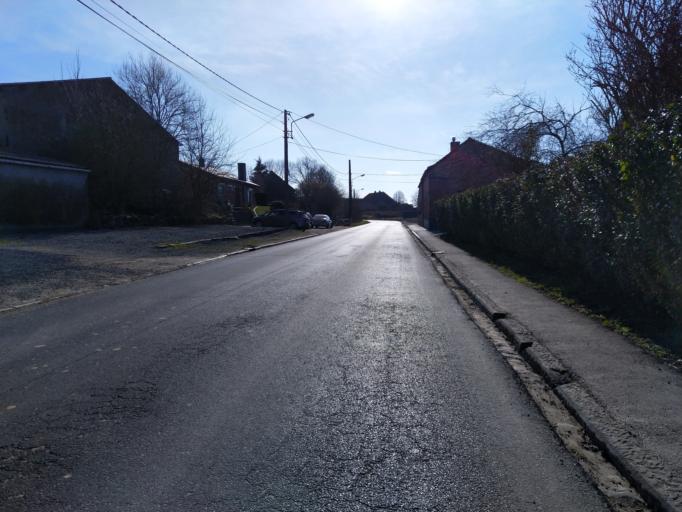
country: BE
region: Wallonia
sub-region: Province du Hainaut
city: Quevy-le-Petit
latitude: 50.3545
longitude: 3.8967
